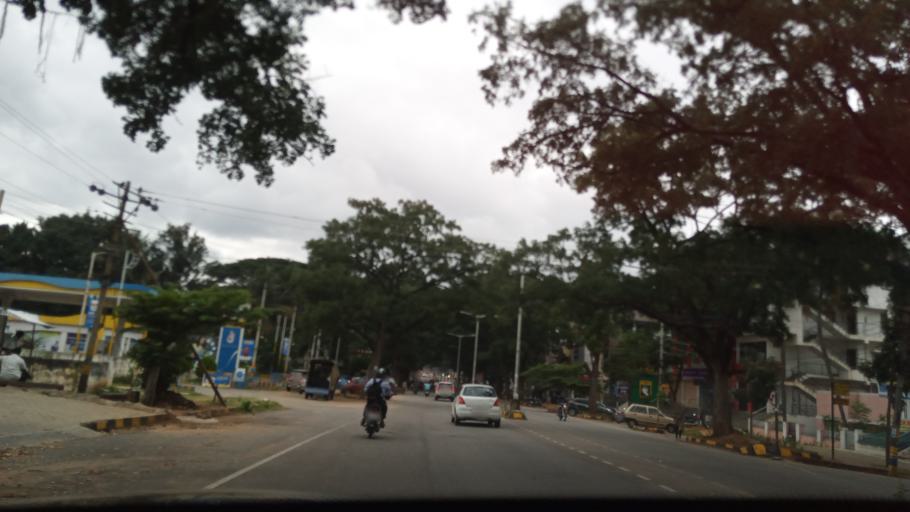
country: IN
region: Karnataka
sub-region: Mysore
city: Mysore
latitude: 12.3022
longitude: 76.6352
